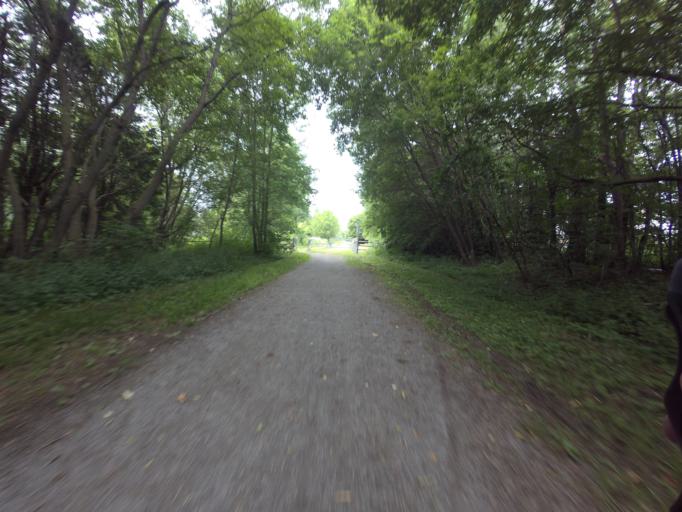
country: CA
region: Ontario
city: Bells Corners
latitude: 45.1417
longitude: -75.6110
